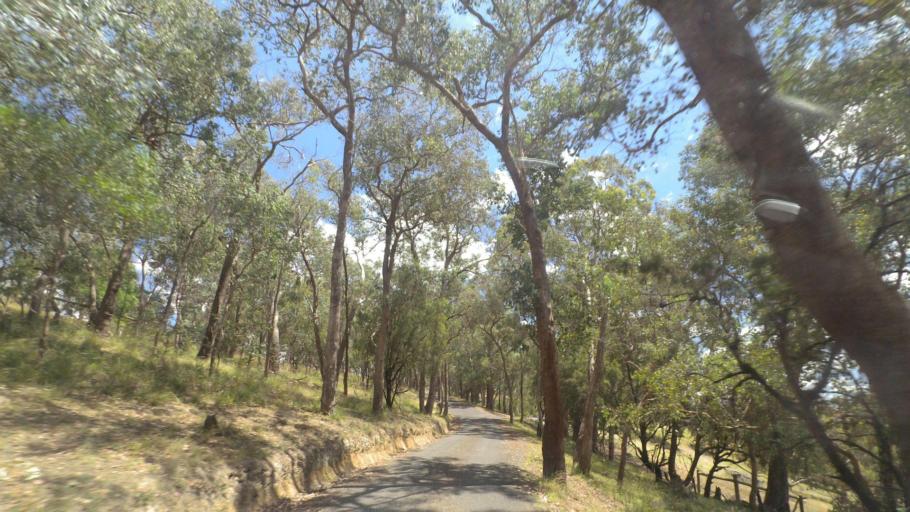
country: AU
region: Victoria
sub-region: Manningham
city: Warrandyte
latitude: -37.7238
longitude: 145.2699
